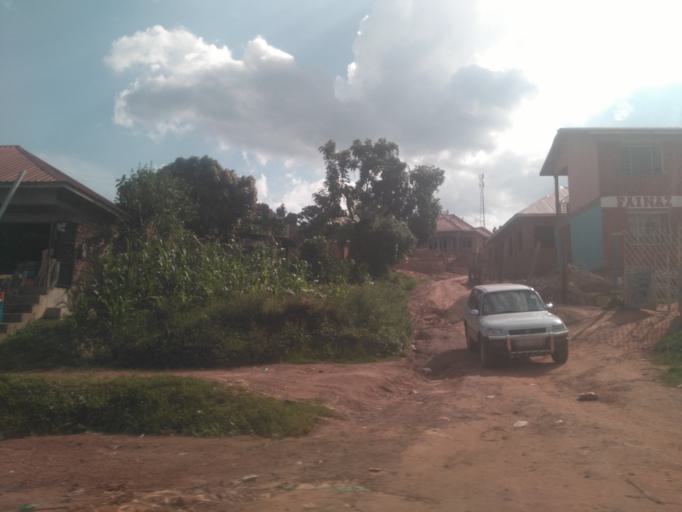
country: UG
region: Central Region
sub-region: Wakiso District
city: Kajansi
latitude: 0.2790
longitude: 32.4731
